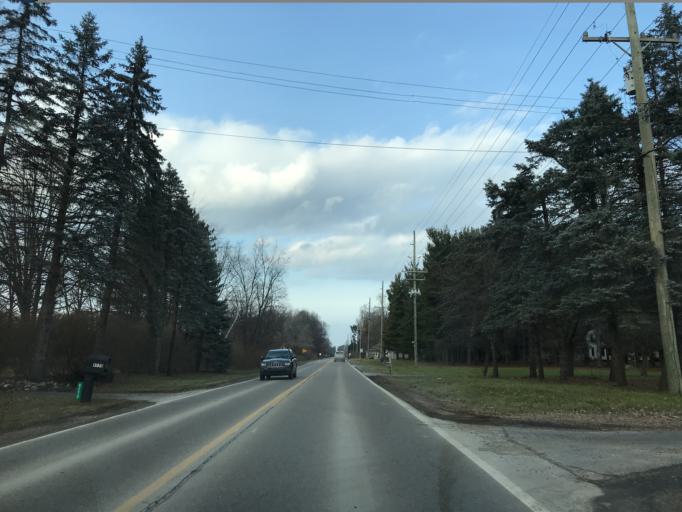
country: US
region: Michigan
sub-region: Oakland County
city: South Lyon
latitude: 42.4618
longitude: -83.6966
